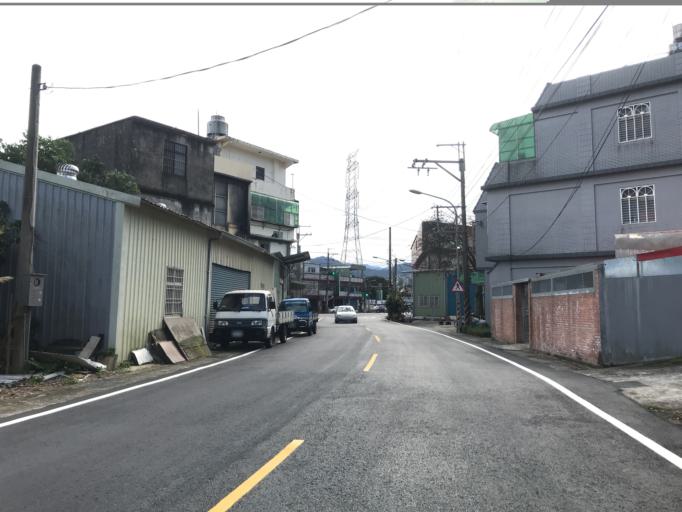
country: TW
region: Taiwan
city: Daxi
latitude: 24.8326
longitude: 121.2440
